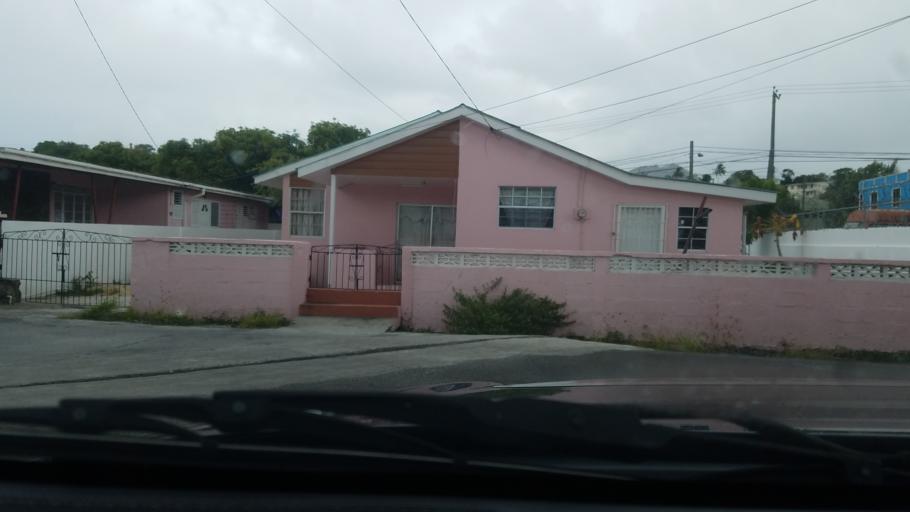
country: LC
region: Castries Quarter
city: Bisee
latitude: 14.0182
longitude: -60.9901
